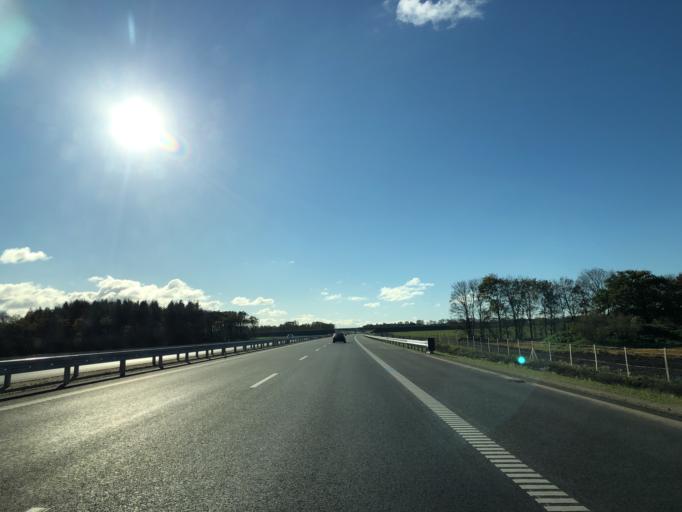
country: DK
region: Central Jutland
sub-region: Herning Kommune
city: Avlum
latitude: 56.3235
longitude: 8.7337
